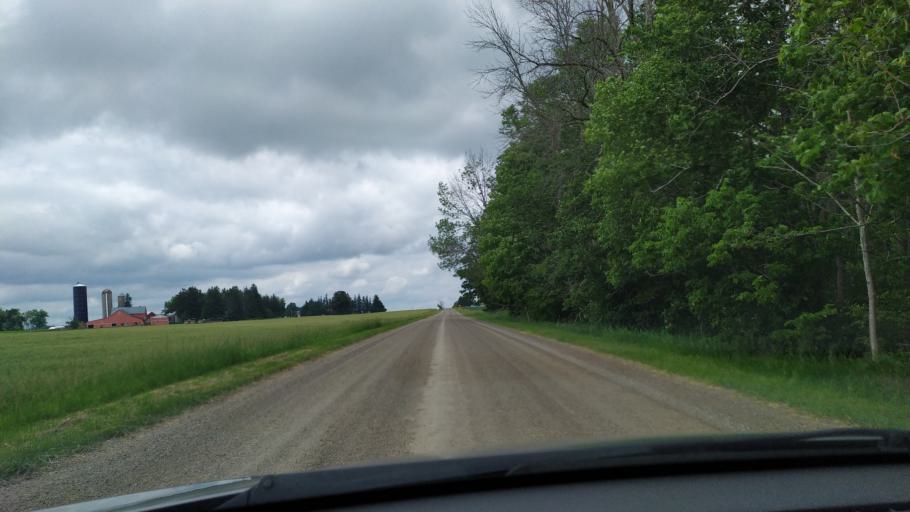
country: CA
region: Ontario
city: Stratford
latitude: 43.4192
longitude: -80.8883
